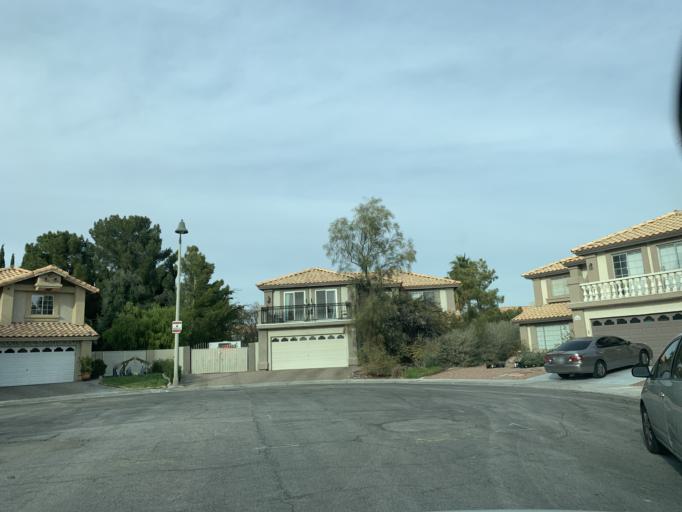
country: US
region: Nevada
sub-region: Clark County
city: Summerlin South
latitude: 36.1422
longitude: -115.3000
